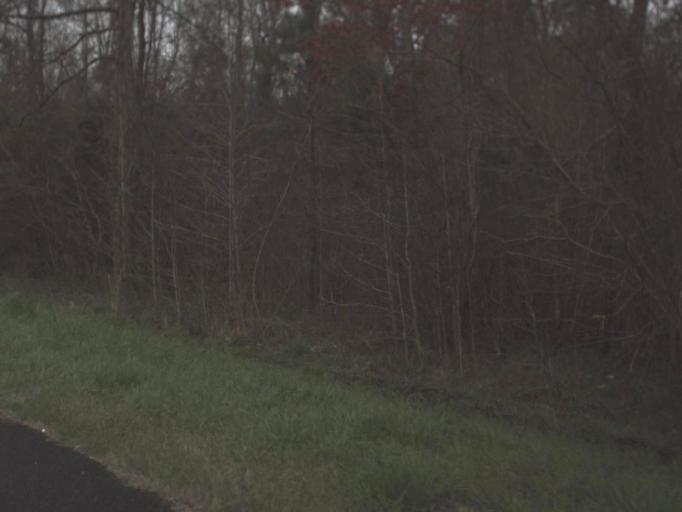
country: US
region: Florida
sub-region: Jefferson County
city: Monticello
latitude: 30.4110
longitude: -83.9227
